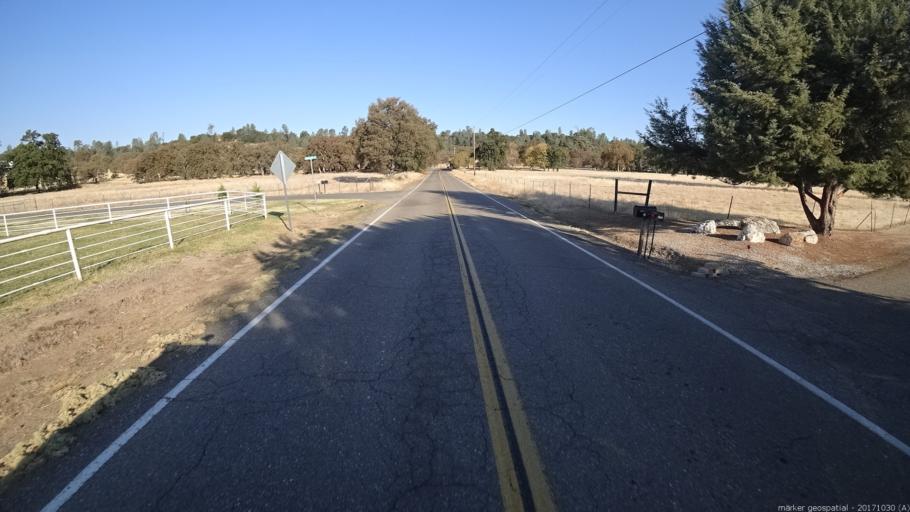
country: US
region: California
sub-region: Shasta County
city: Palo Cedro
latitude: 40.5680
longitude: -122.1924
